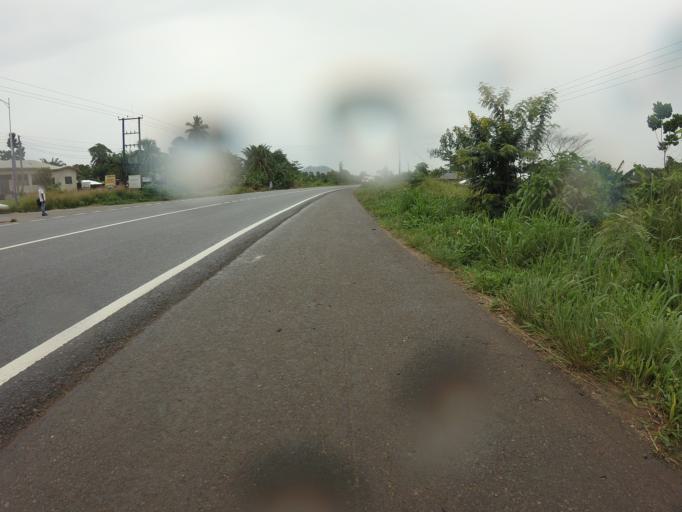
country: GH
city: Kibi
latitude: 6.1605
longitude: -0.4836
